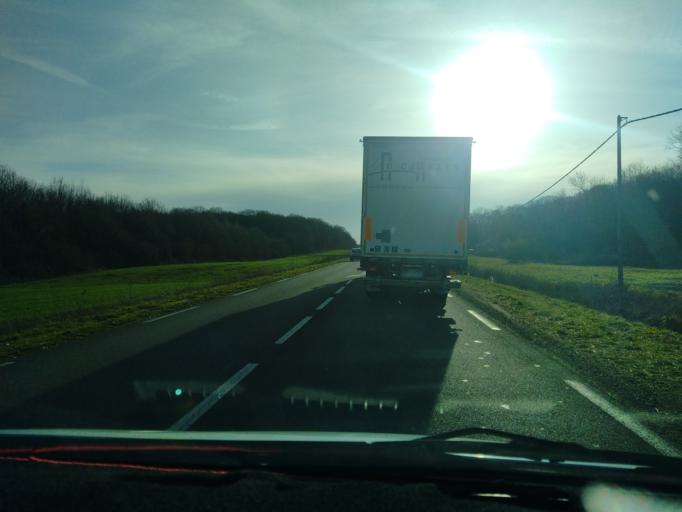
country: FR
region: Franche-Comte
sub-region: Departement de la Haute-Saone
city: Gray
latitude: 47.4266
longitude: 5.6110
